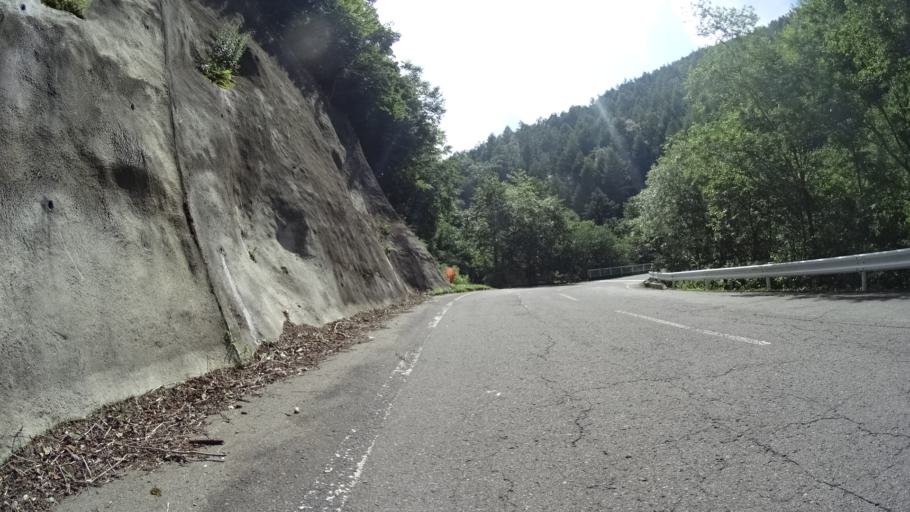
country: JP
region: Nagano
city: Saku
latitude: 36.0529
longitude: 138.3939
